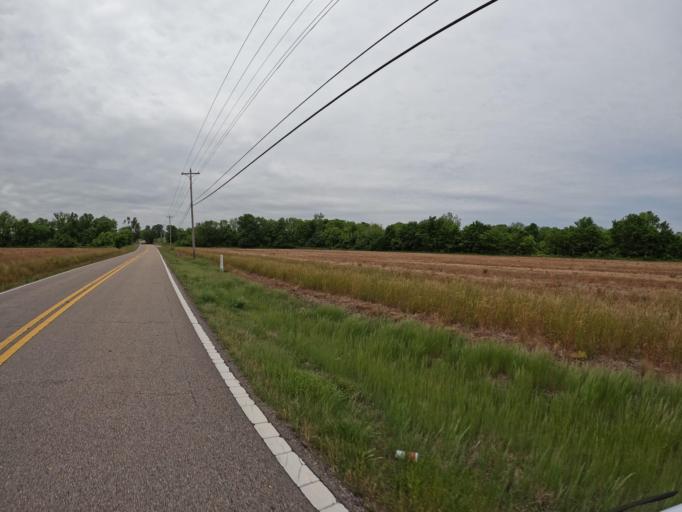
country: US
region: Mississippi
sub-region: Lee County
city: Tupelo
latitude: 34.2925
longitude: -88.7642
